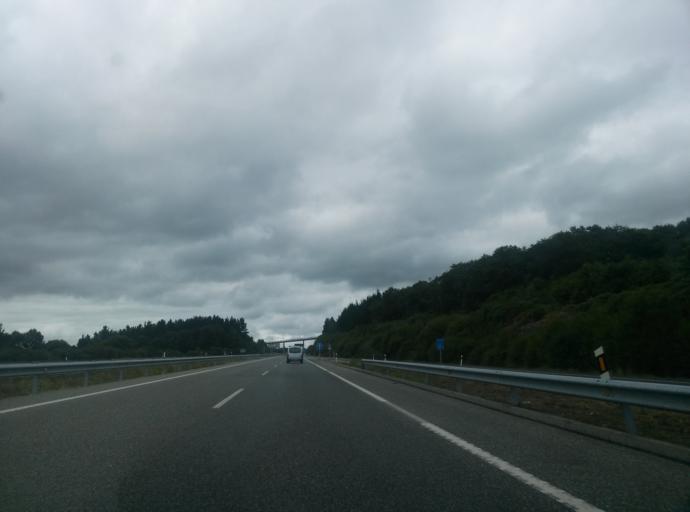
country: ES
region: Galicia
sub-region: Provincia de Lugo
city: Vilalba
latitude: 43.3033
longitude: -7.7026
